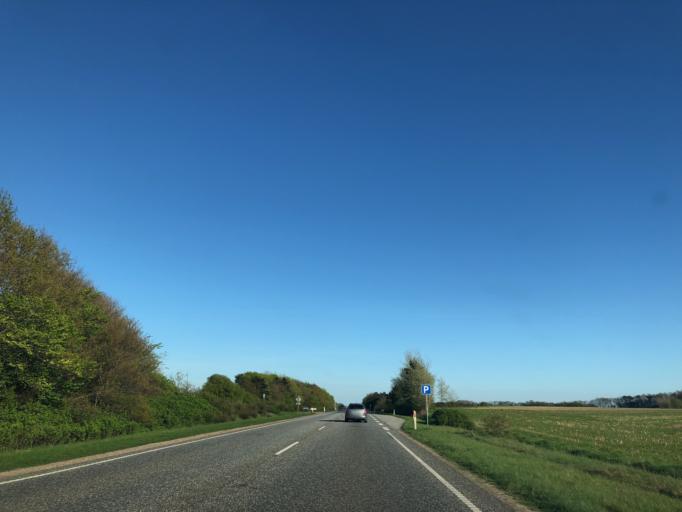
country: DK
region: Central Jutland
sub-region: Herning Kommune
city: Avlum
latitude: 56.3006
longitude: 8.7148
